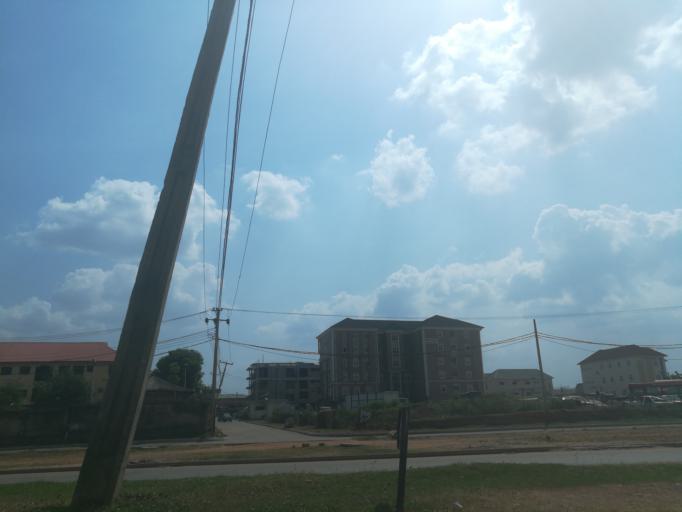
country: NG
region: Abuja Federal Capital Territory
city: Abuja
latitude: 9.0541
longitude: 7.4422
